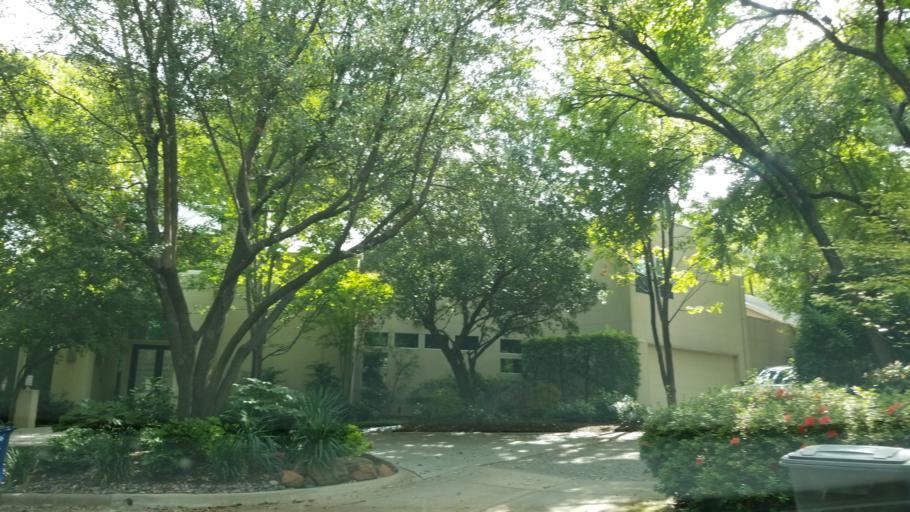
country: US
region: Texas
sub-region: Dallas County
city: Addison
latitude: 32.9348
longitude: -96.8013
